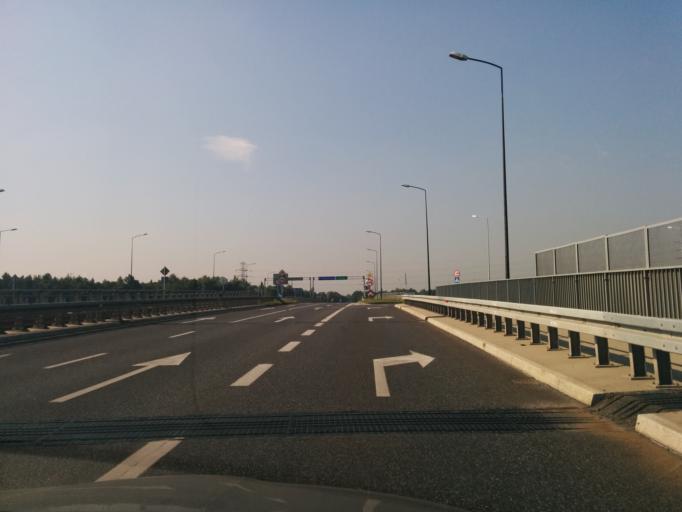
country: PL
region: Silesian Voivodeship
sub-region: Powiat gliwicki
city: Paniowki
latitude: 50.2625
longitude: 18.7978
